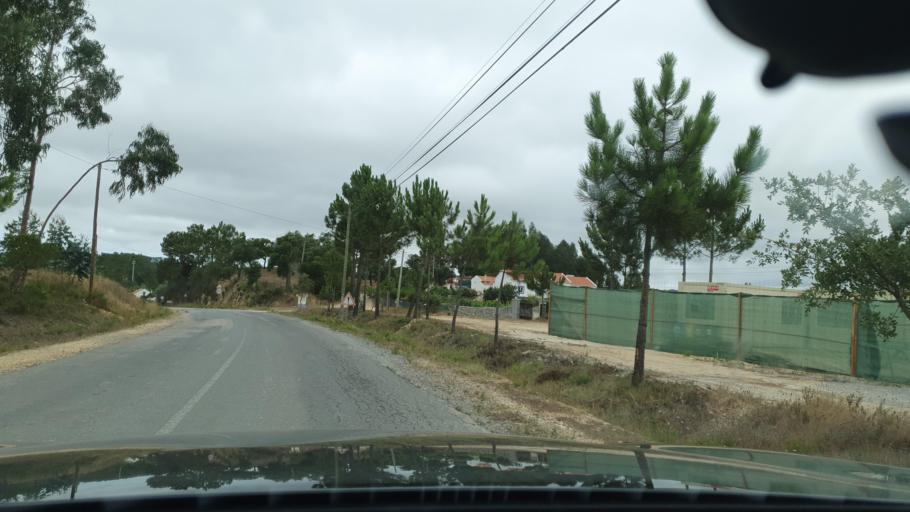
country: PT
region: Beja
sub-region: Odemira
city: Sao Teotonio
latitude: 37.5050
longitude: -8.6918
